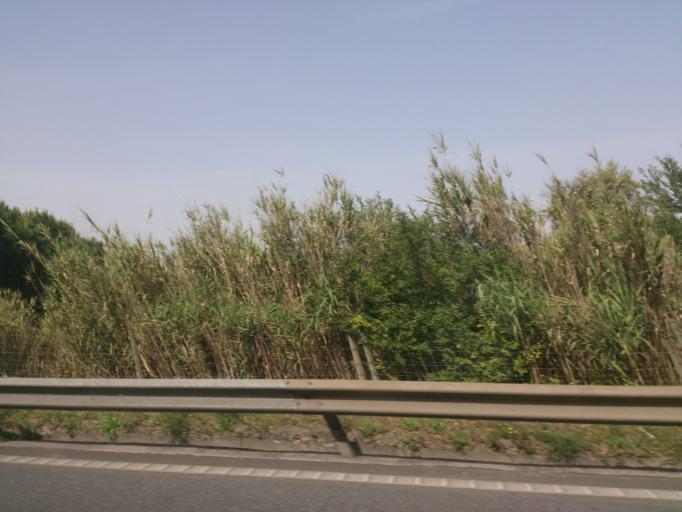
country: PT
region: Lisbon
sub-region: Loures
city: Bobadela
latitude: 38.8025
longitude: -9.1073
